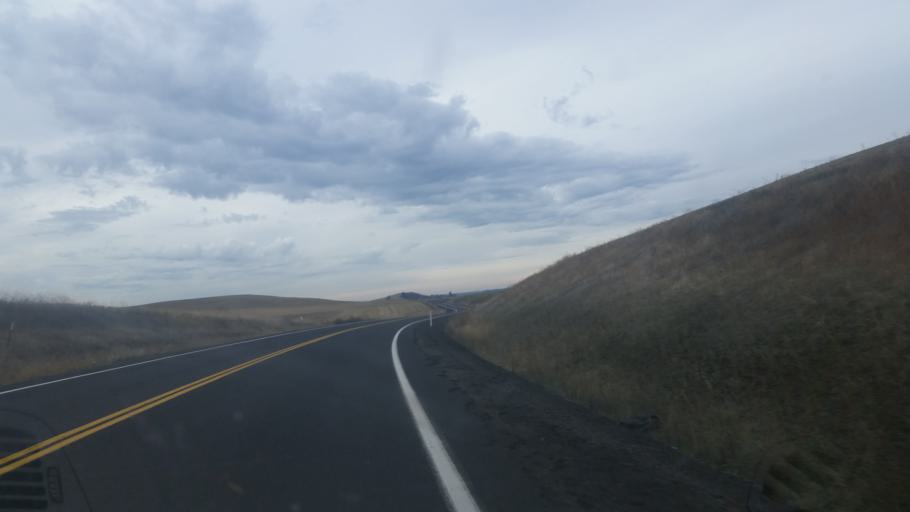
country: US
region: Washington
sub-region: Spokane County
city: Cheney
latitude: 47.3907
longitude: -117.4195
